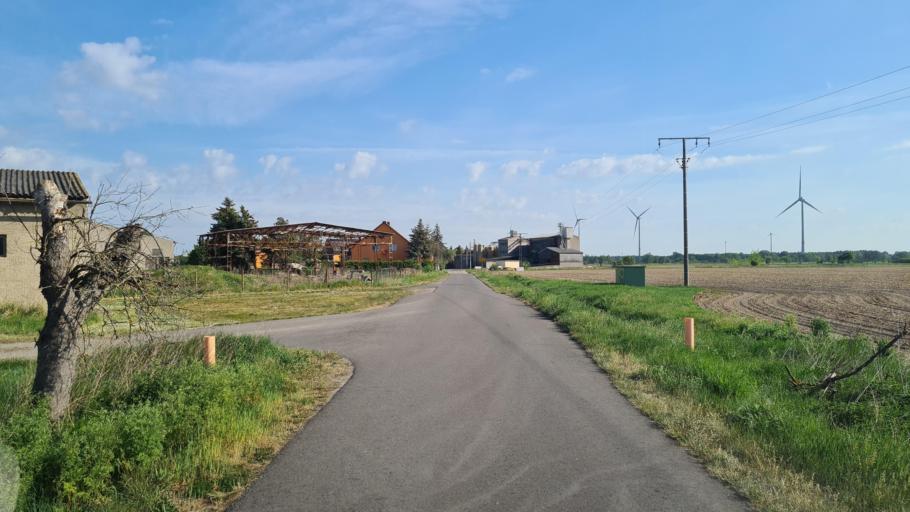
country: DE
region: Brandenburg
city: Falkenberg
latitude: 51.6146
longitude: 13.2055
